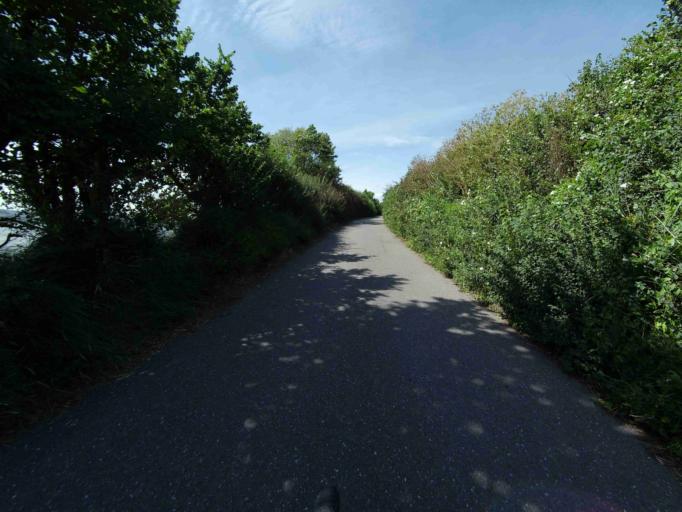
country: GB
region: England
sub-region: Devon
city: Starcross
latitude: 50.6438
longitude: -3.4296
